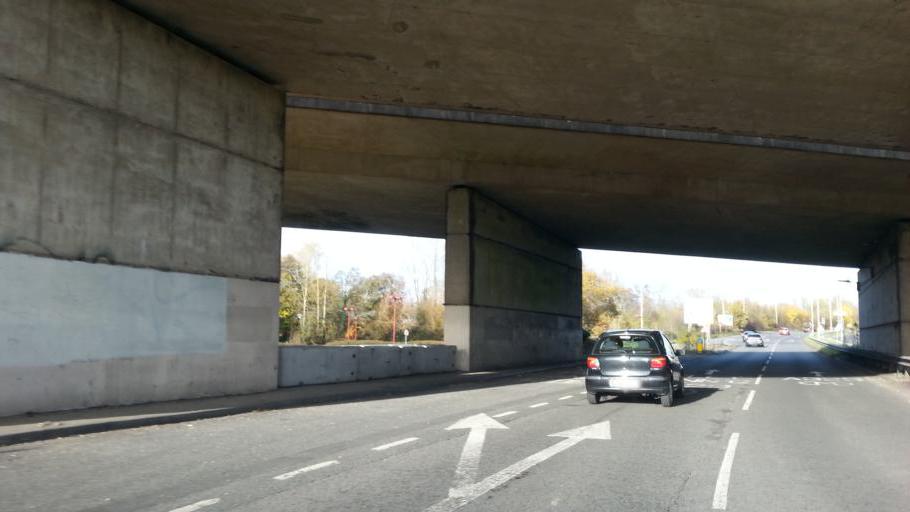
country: GB
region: England
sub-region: Wokingham
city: Woodley
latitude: 51.4390
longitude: -0.8958
